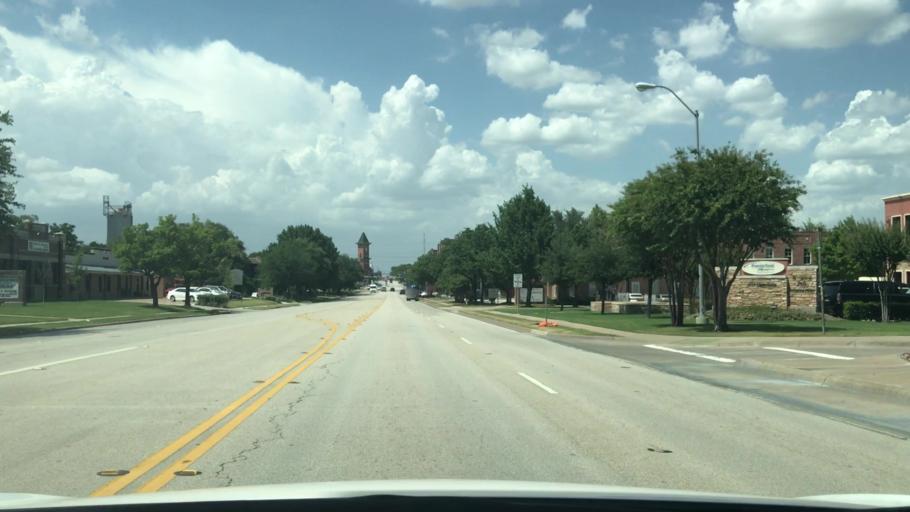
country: US
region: Texas
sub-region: Tarrant County
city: Grapevine
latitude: 32.9292
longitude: -97.0784
